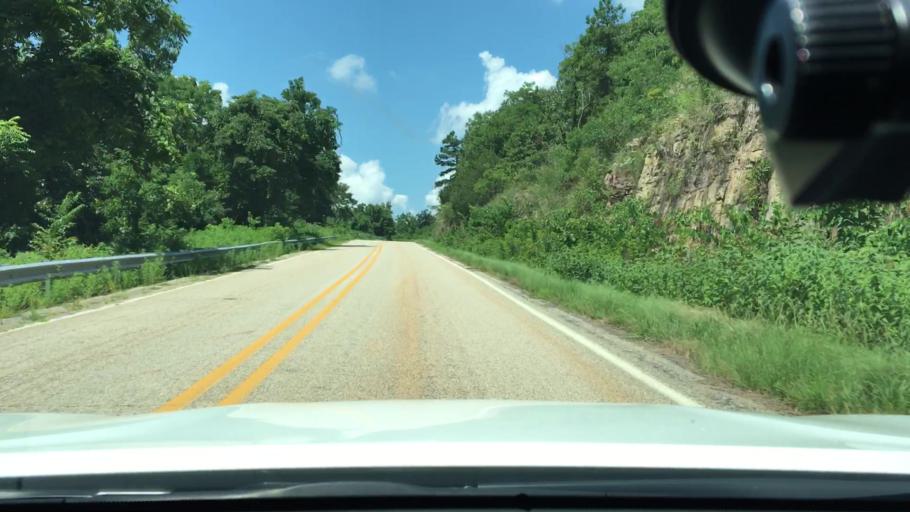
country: US
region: Arkansas
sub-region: Logan County
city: Paris
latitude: 35.1765
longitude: -93.5878
